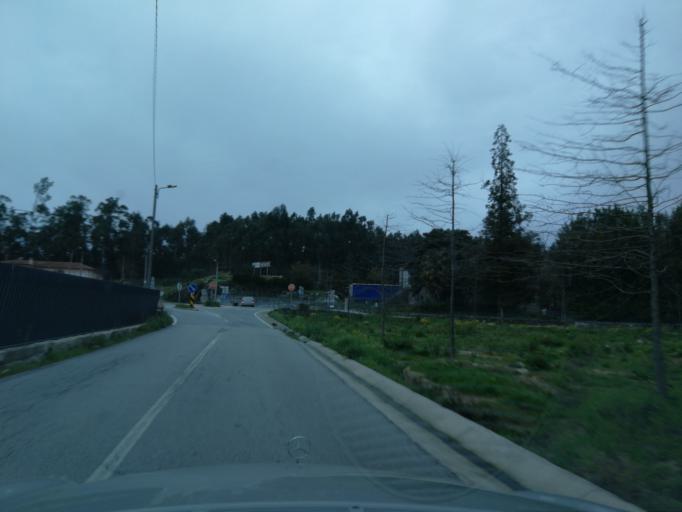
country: PT
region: Braga
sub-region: Braga
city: Oliveira
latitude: 41.4873
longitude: -8.4731
